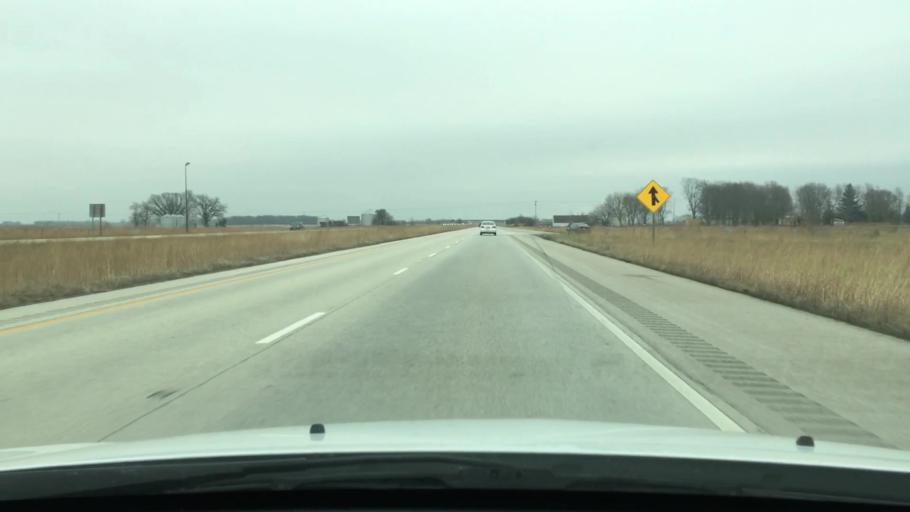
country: US
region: Illinois
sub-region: Sangamon County
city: New Berlin
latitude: 39.7401
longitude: -89.9207
